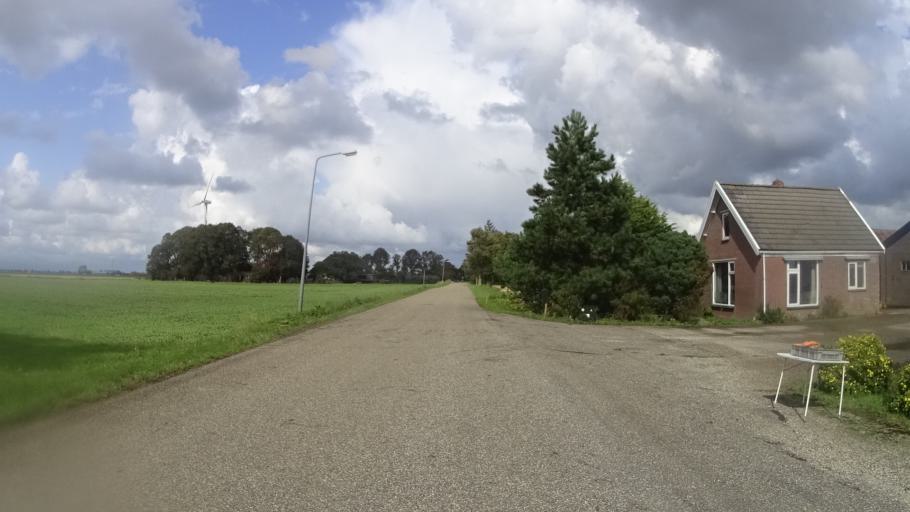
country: NL
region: North Holland
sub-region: Gemeente Schagen
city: Schagen
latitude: 52.8442
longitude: 4.8740
